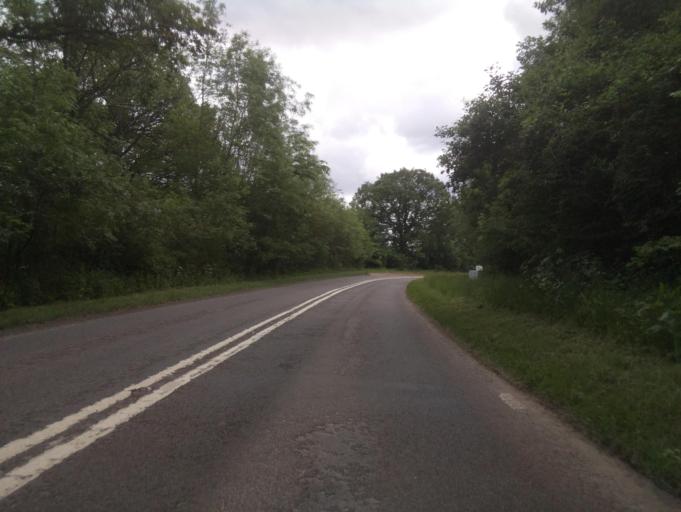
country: GB
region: England
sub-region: Herefordshire
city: Yatton
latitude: 51.9582
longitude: -2.5255
